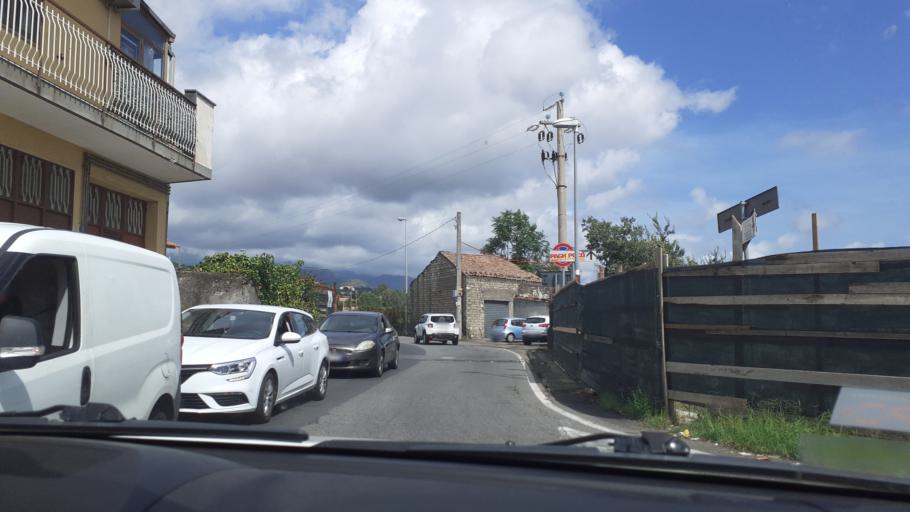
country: IT
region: Sicily
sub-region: Catania
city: San Giovanni la Punta
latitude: 37.5875
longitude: 15.0949
